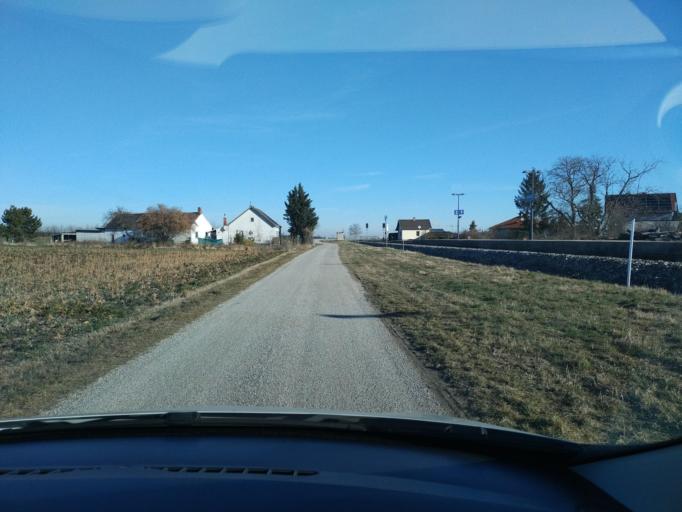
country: AT
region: Lower Austria
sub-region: Politischer Bezirk Wiener Neustadt
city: Lanzenkirchen
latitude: 47.7515
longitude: 16.2422
